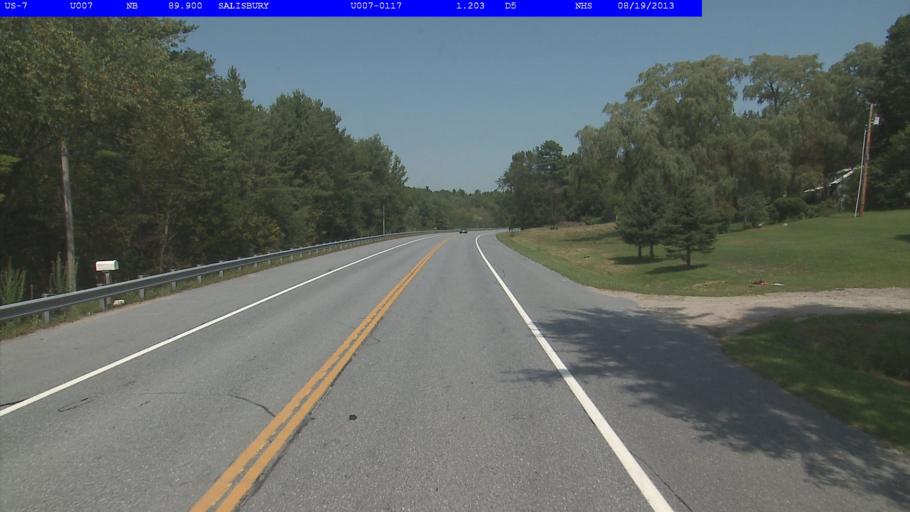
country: US
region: Vermont
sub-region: Rutland County
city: Brandon
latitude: 43.9092
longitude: -73.1109
